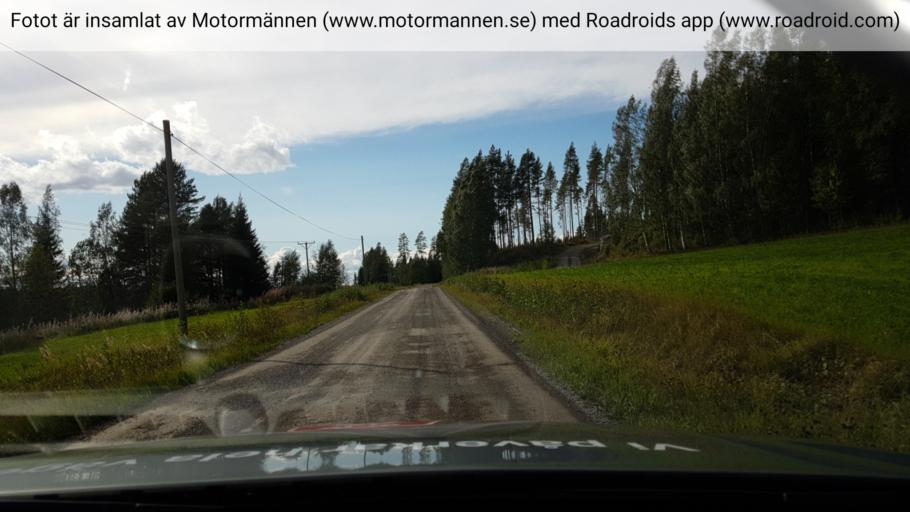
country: SE
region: Jaemtland
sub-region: Braecke Kommun
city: Braecke
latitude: 63.1970
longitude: 15.4697
